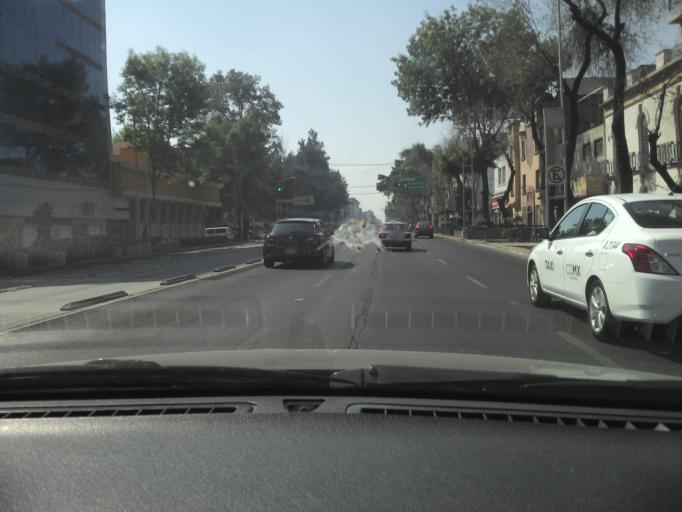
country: MX
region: Mexico City
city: Cuauhtemoc
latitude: 19.4235
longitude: -99.1539
